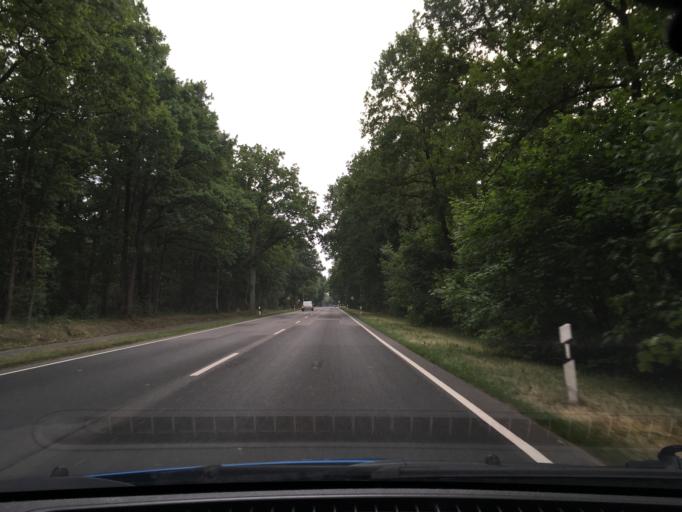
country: DE
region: Lower Saxony
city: Tostedt
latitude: 53.2975
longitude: 9.7409
